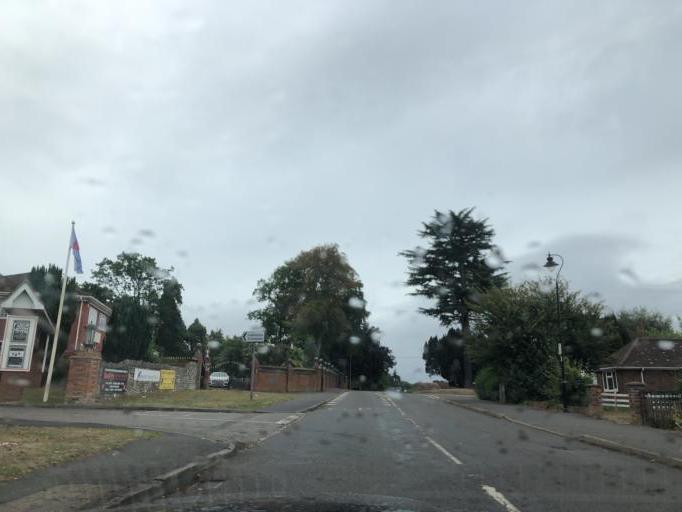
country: GB
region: England
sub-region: Surrey
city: Frimley
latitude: 51.3036
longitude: -0.7224
